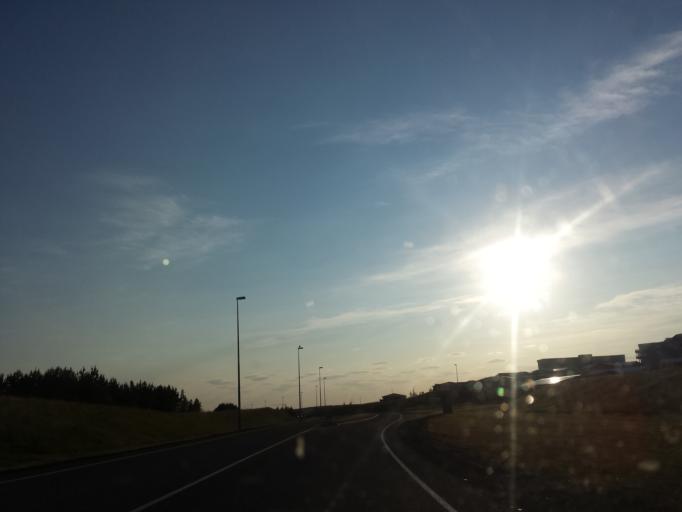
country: IS
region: Capital Region
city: Reykjavik
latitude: 64.0890
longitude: -21.8405
